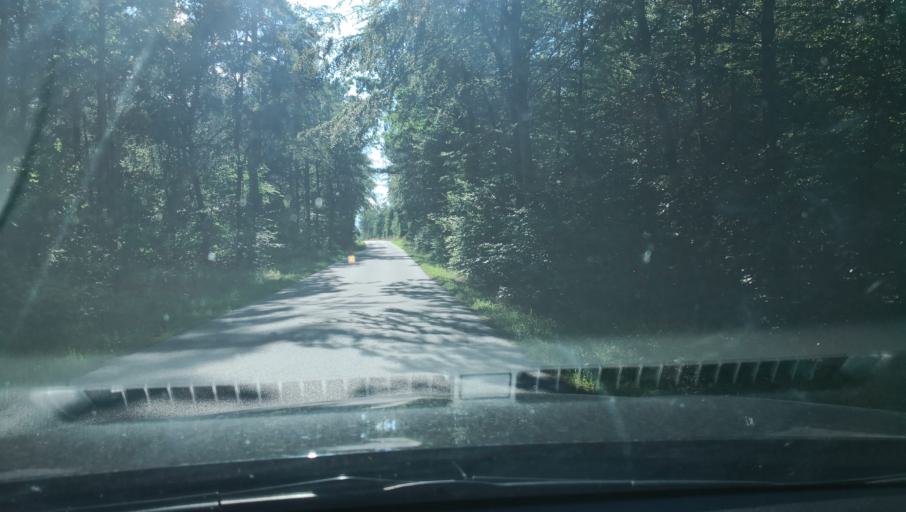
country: SE
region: Skane
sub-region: Kristianstads Kommun
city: Degeberga
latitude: 55.7689
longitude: 14.1675
